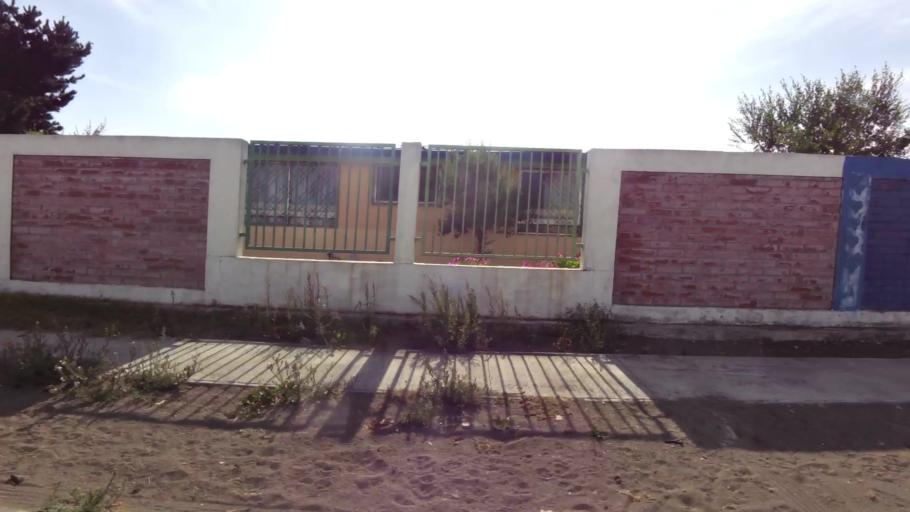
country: CL
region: Biobio
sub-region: Provincia de Concepcion
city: Talcahuano
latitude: -36.7817
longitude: -73.1122
